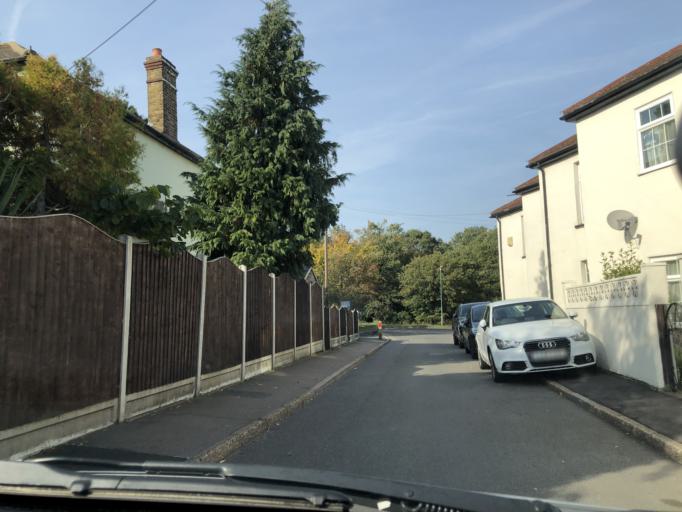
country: GB
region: England
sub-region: Kent
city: Dartford
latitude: 51.4314
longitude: 0.1858
